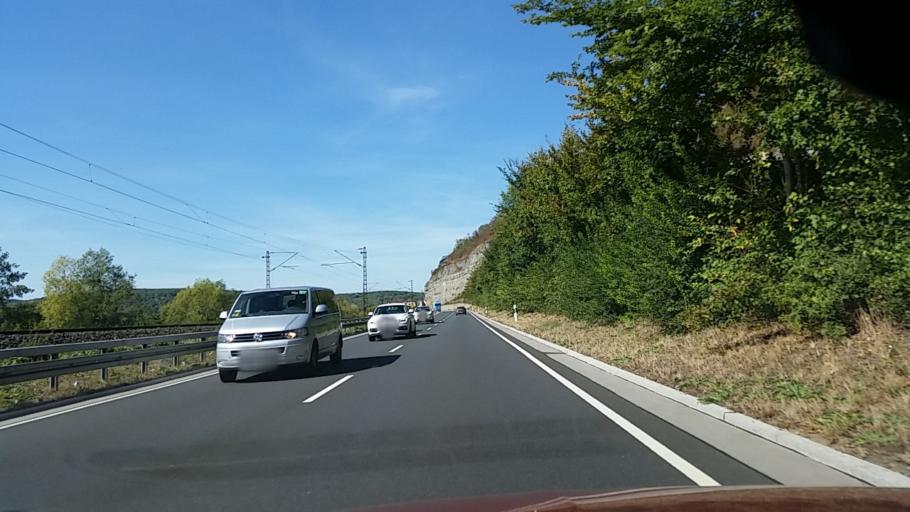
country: DE
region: Bavaria
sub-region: Regierungsbezirk Unterfranken
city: Zellingen
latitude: 49.8985
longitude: 9.8284
